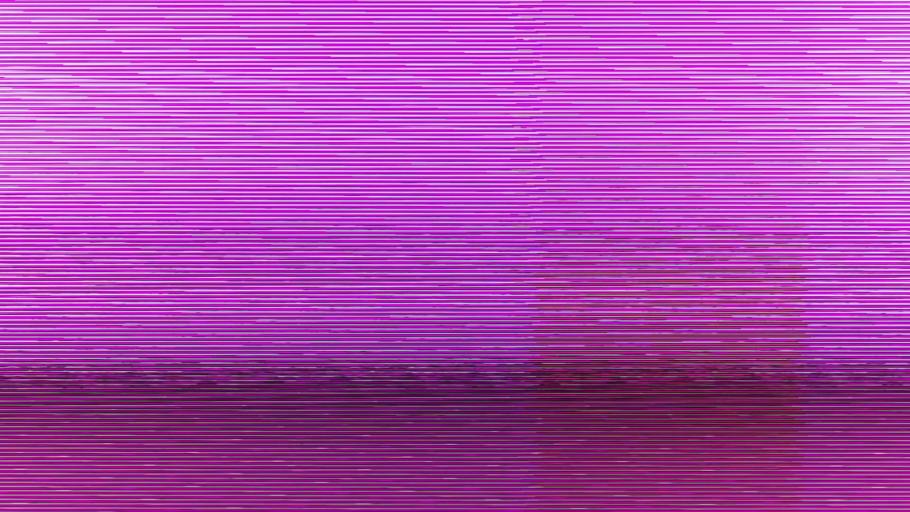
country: US
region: Michigan
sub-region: Macomb County
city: Romeo
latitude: 42.7599
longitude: -83.0110
